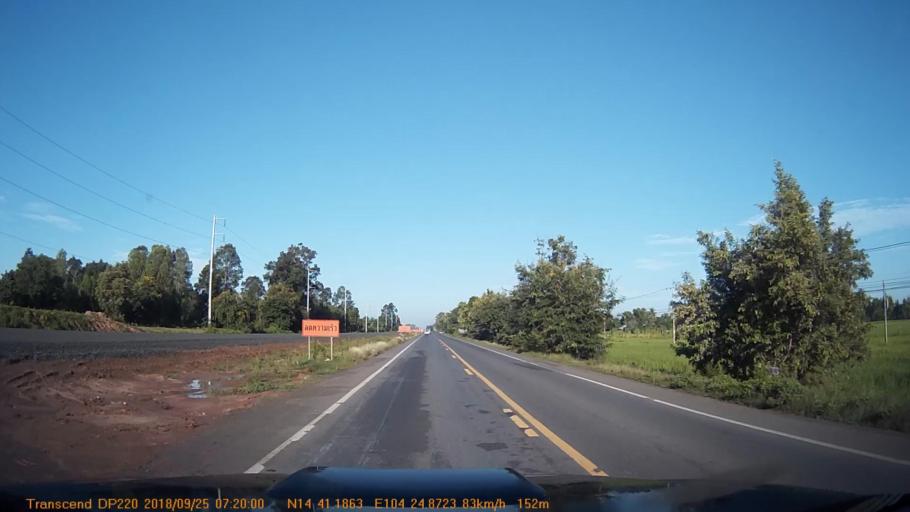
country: TH
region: Sisaket
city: Khun Han
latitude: 14.6864
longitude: 104.4143
